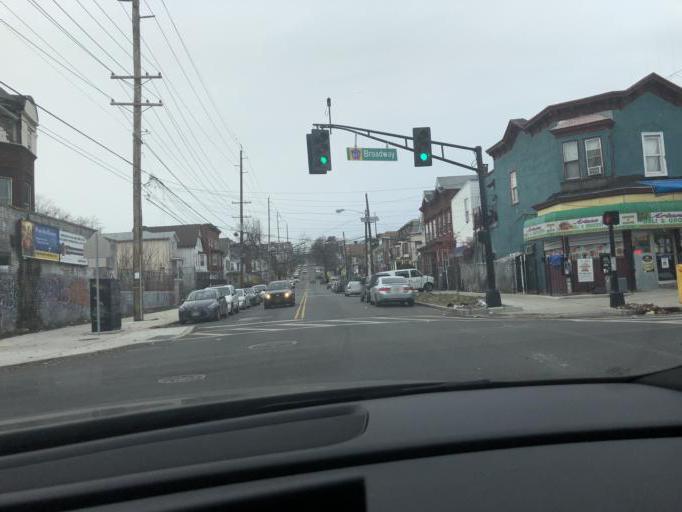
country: US
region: New Jersey
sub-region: Hudson County
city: East Newark
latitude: 40.7590
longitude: -74.1690
